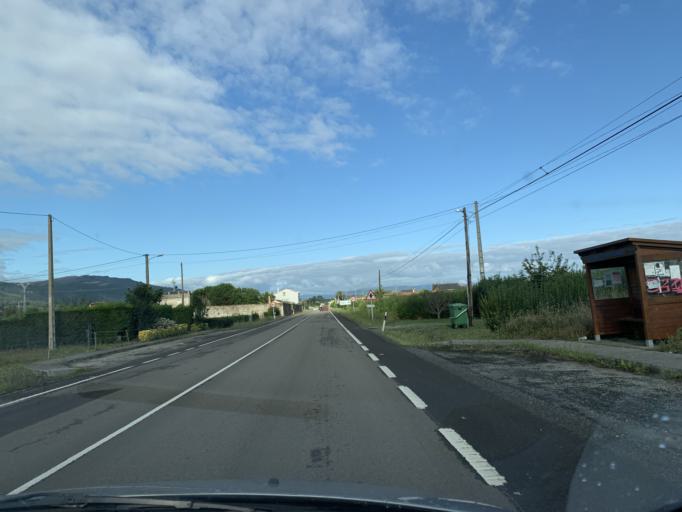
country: ES
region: Galicia
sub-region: Provincia de Lugo
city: Ribadeo
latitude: 43.5465
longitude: -7.1007
